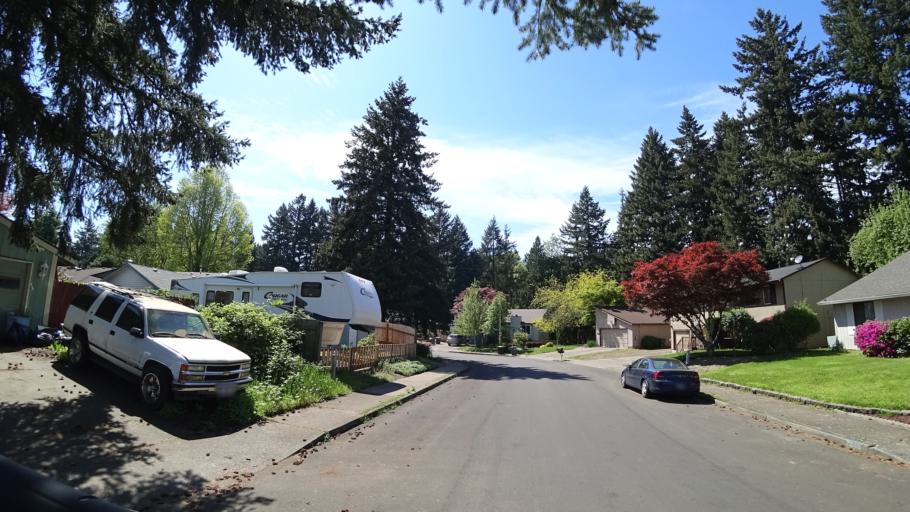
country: US
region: Oregon
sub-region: Washington County
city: Hillsboro
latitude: 45.5170
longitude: -122.9533
